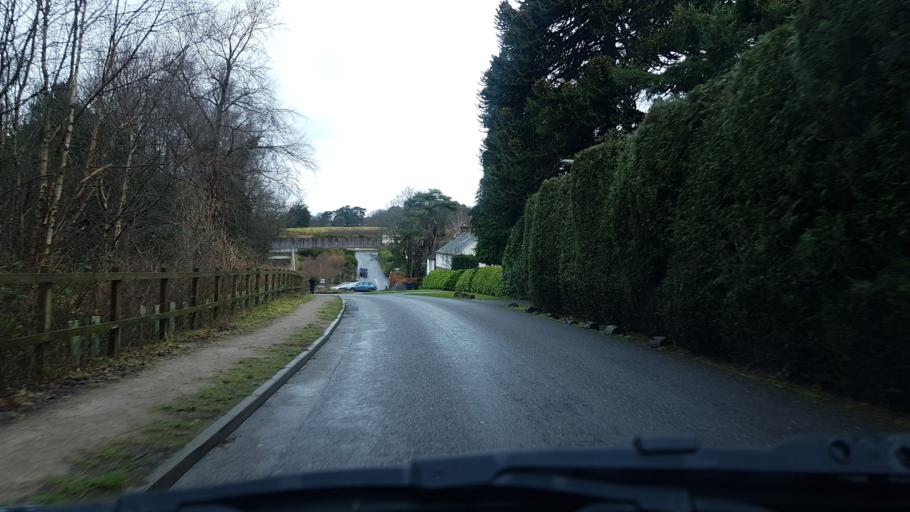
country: GB
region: England
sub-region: Surrey
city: Hindhead
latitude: 51.0968
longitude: -0.7548
